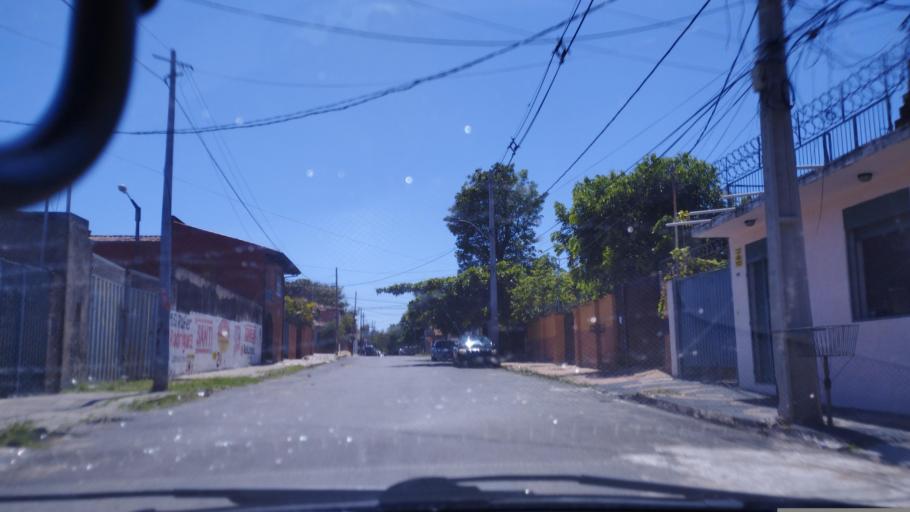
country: PY
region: Asuncion
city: Asuncion
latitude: -25.2969
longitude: -57.6642
